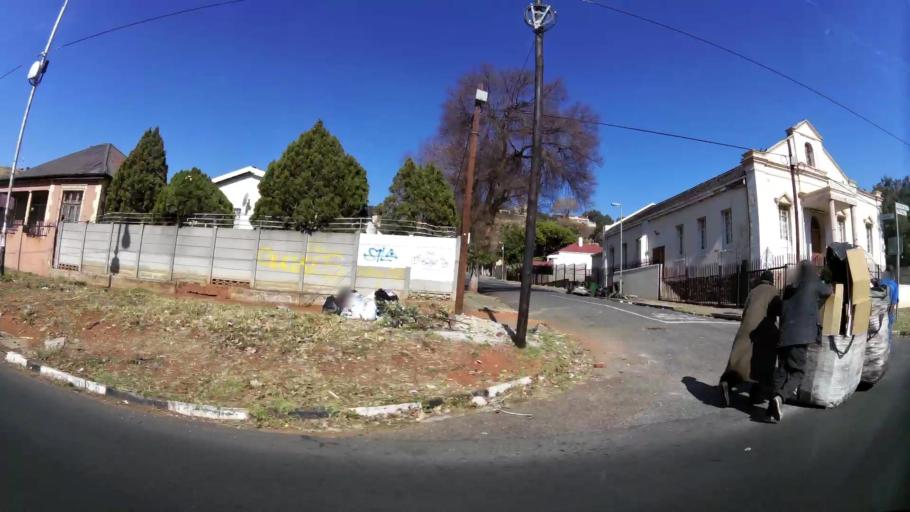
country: ZA
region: Gauteng
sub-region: City of Johannesburg Metropolitan Municipality
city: Johannesburg
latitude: -26.1938
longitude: 28.0782
